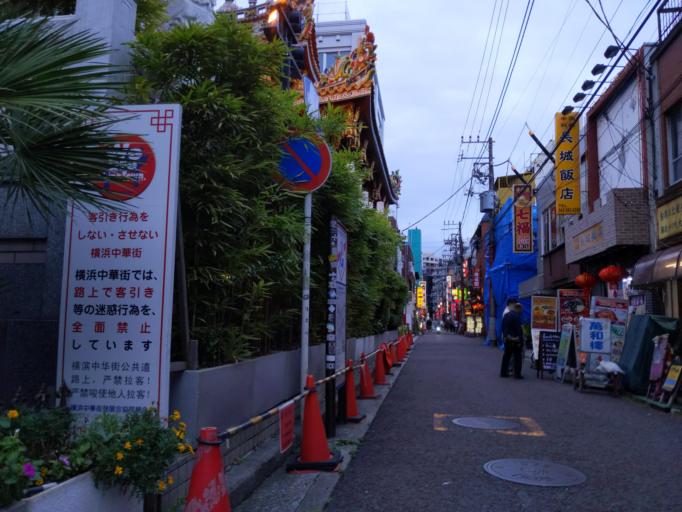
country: JP
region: Kanagawa
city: Yokohama
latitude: 35.4421
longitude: 139.6453
